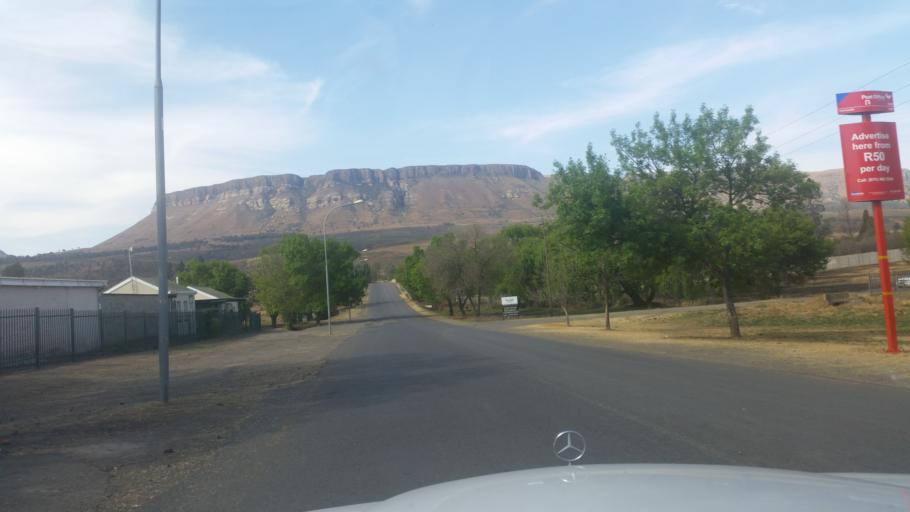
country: ZA
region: Orange Free State
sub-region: Thabo Mofutsanyana District Municipality
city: Harrismith
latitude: -28.2690
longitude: 29.1317
